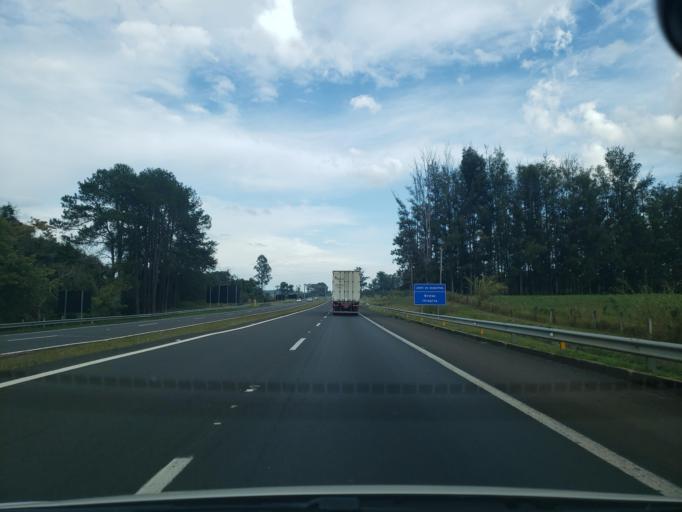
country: BR
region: Sao Paulo
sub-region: Itirapina
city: Itirapina
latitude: -22.2648
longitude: -47.9115
